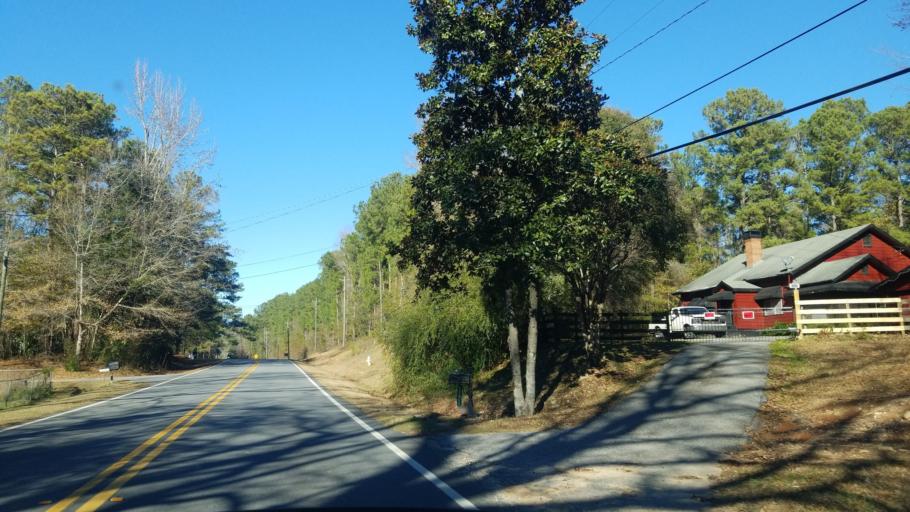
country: US
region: Georgia
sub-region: Harris County
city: Hamilton
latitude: 32.6598
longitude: -84.8673
